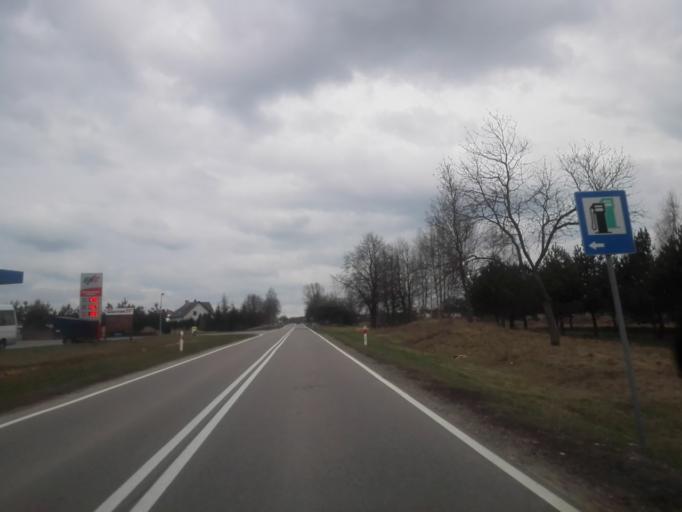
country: PL
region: Podlasie
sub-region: Powiat sejnenski
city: Sejny
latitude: 54.0466
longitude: 23.3555
